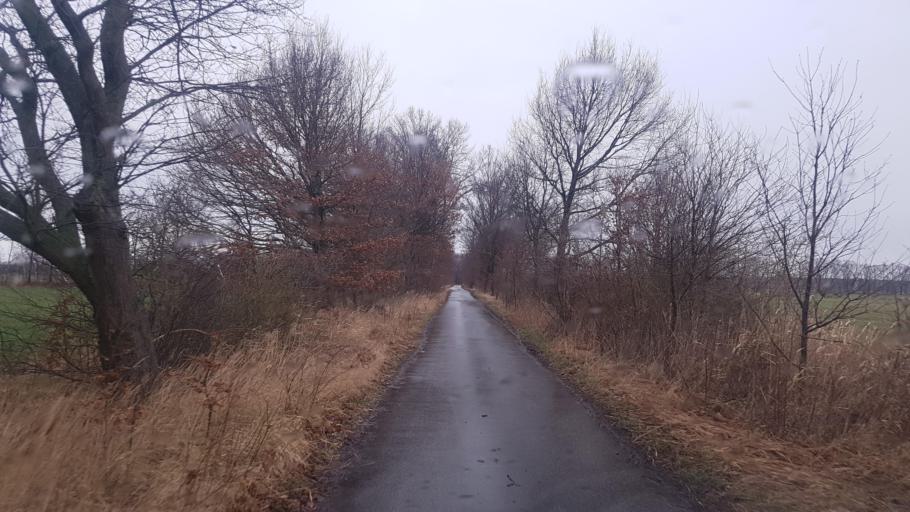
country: DE
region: Brandenburg
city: Grossthiemig
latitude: 51.4221
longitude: 13.6504
